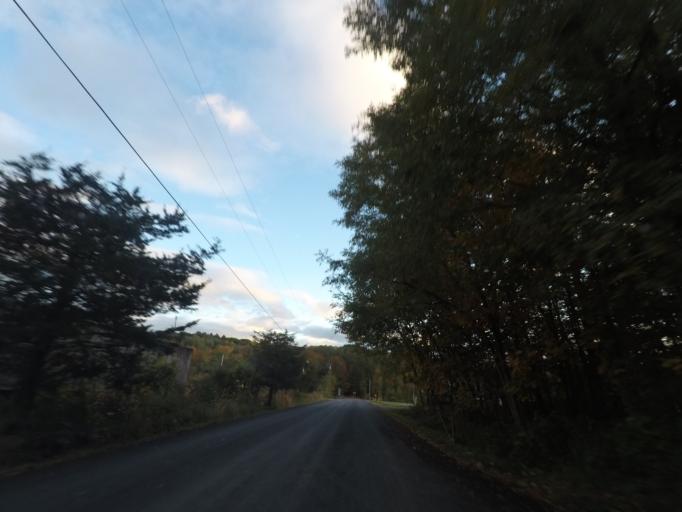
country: US
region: New York
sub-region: Rensselaer County
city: Nassau
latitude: 42.5189
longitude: -73.5902
